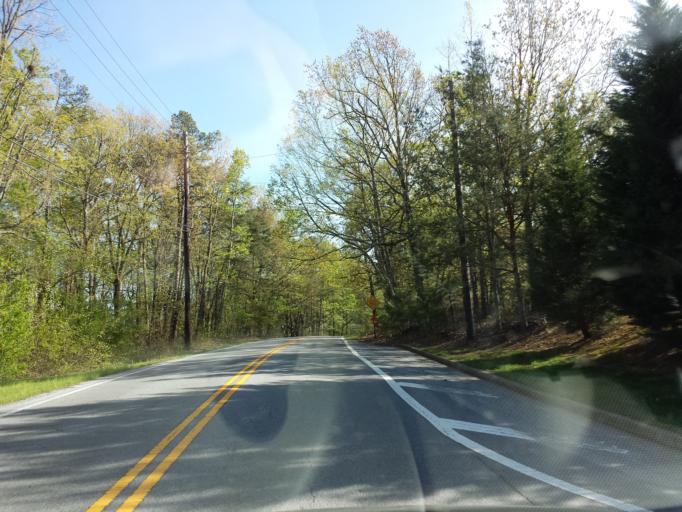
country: US
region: Georgia
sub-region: Cobb County
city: Marietta
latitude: 33.9746
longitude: -84.4997
